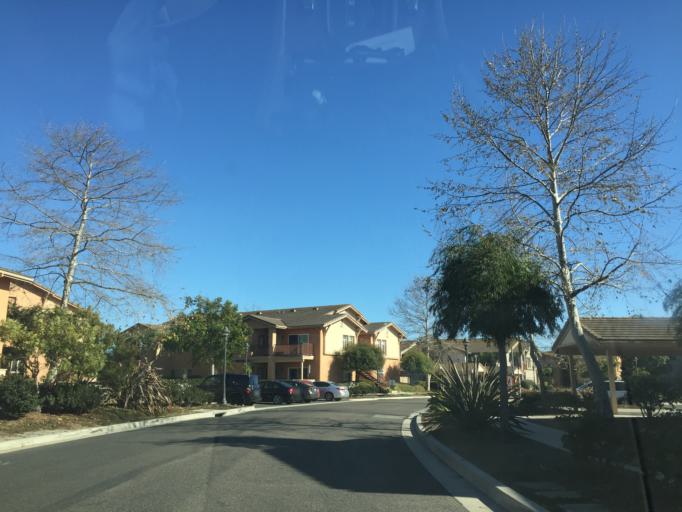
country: US
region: California
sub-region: Santa Barbara County
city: Isla Vista
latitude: 34.4334
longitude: -119.8510
